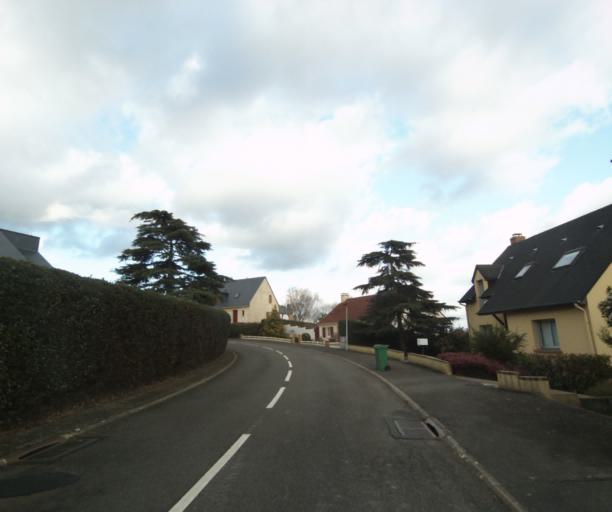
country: FR
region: Pays de la Loire
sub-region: Departement de la Sarthe
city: Allonnes
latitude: 47.9870
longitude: 0.1614
